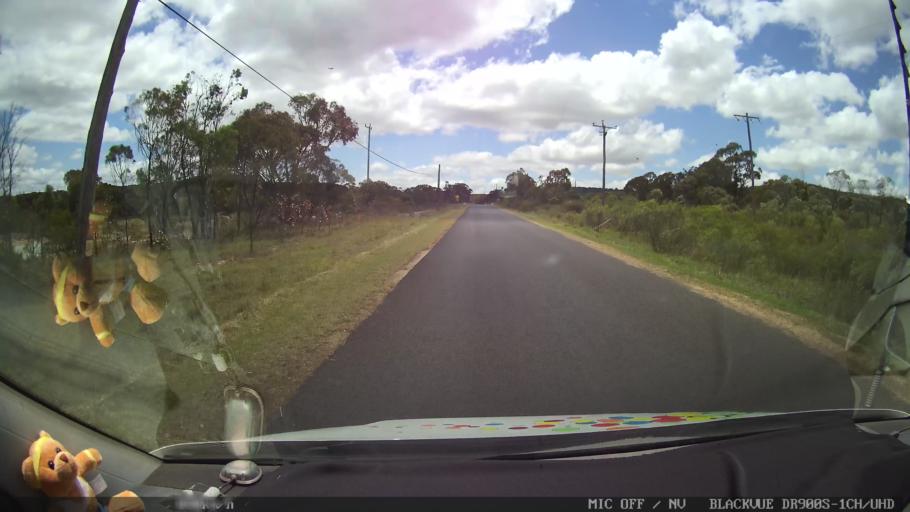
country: AU
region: New South Wales
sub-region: Glen Innes Severn
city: Glen Innes
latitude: -29.4426
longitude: 151.6080
